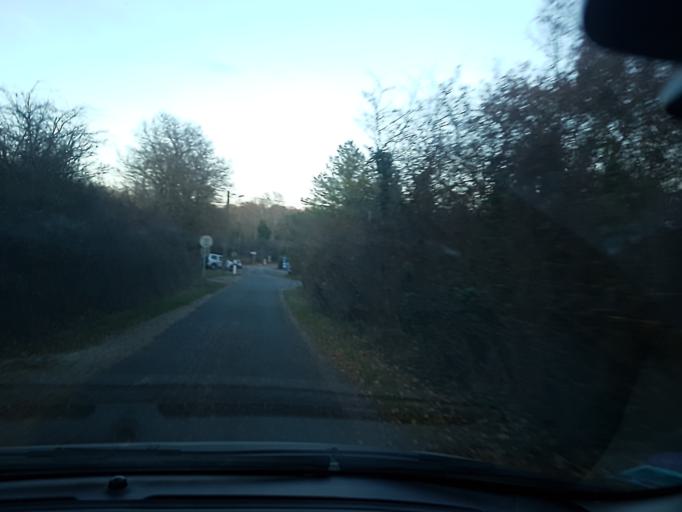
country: FR
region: Rhone-Alpes
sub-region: Departement du Rhone
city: Vourles
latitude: 45.6495
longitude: 4.7661
